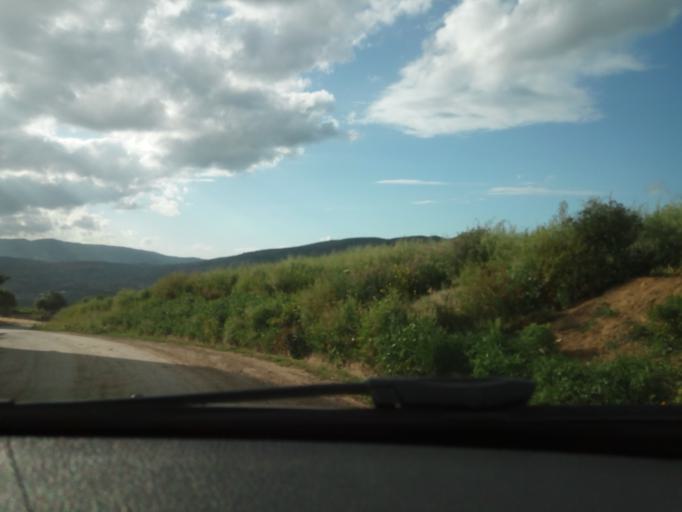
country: DZ
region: Tipaza
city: El Affroun
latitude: 36.3731
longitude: 2.4991
